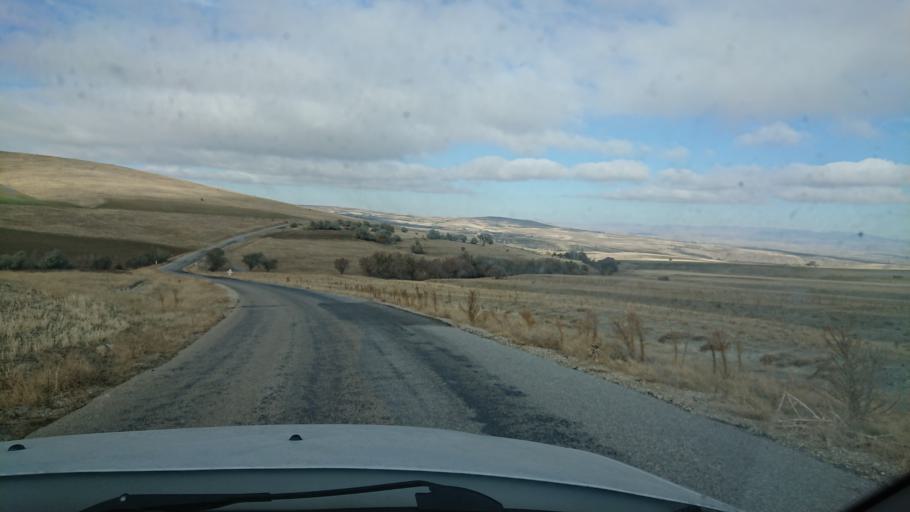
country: TR
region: Aksaray
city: Ortakoy
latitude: 38.7881
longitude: 34.0008
